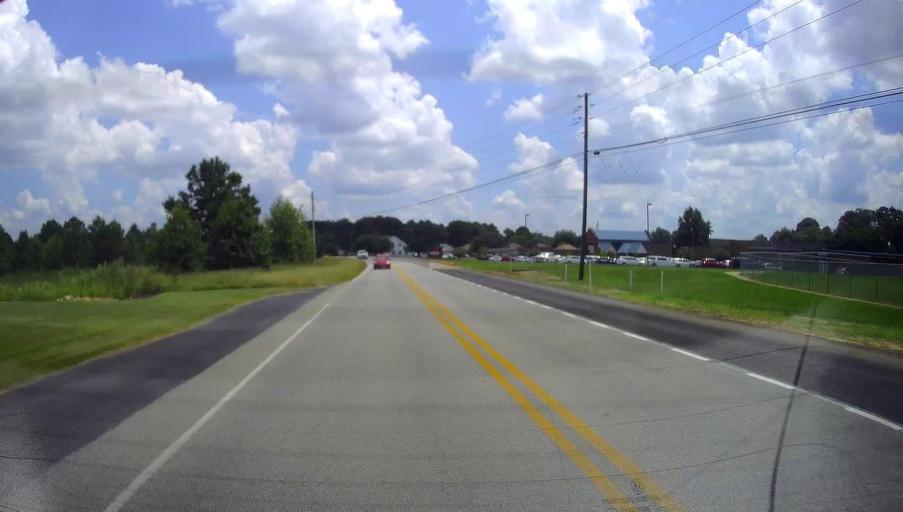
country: US
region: Georgia
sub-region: Houston County
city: Centerville
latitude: 32.6100
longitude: -83.6893
